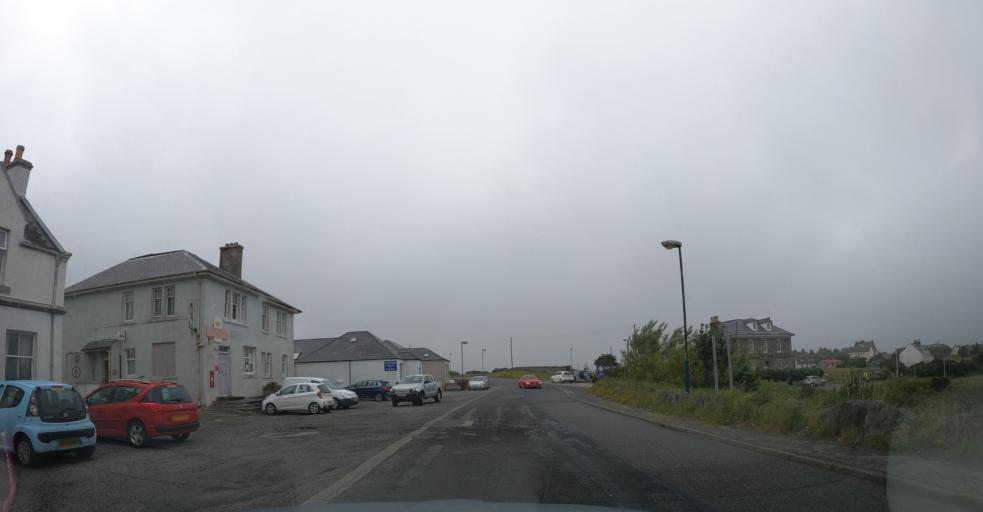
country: GB
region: Scotland
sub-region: Eilean Siar
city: Isle of North Uist
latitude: 57.6015
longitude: -7.1632
